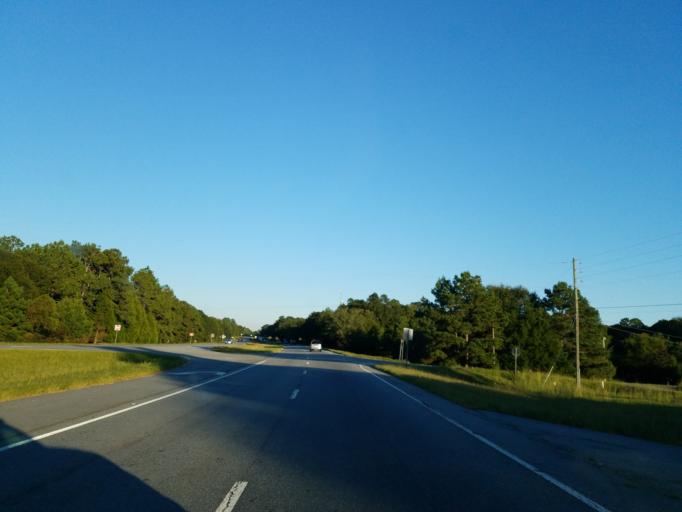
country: US
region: Georgia
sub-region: Tift County
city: Omega
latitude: 31.4748
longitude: -83.6694
